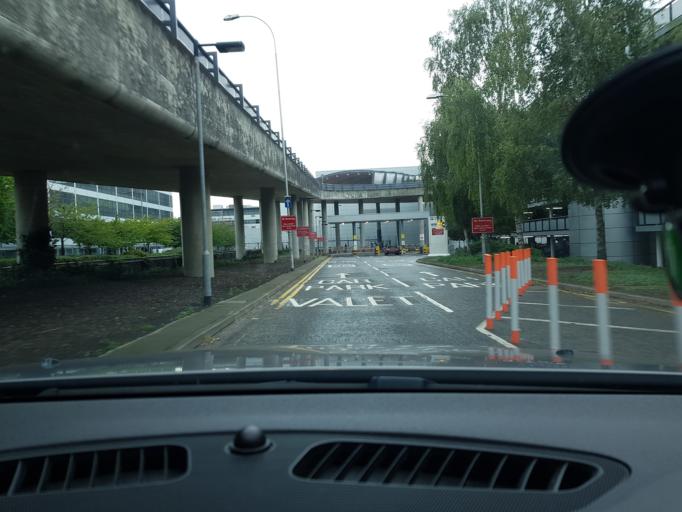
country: GB
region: England
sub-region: Surrey
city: Horley
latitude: 51.1603
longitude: -0.1743
